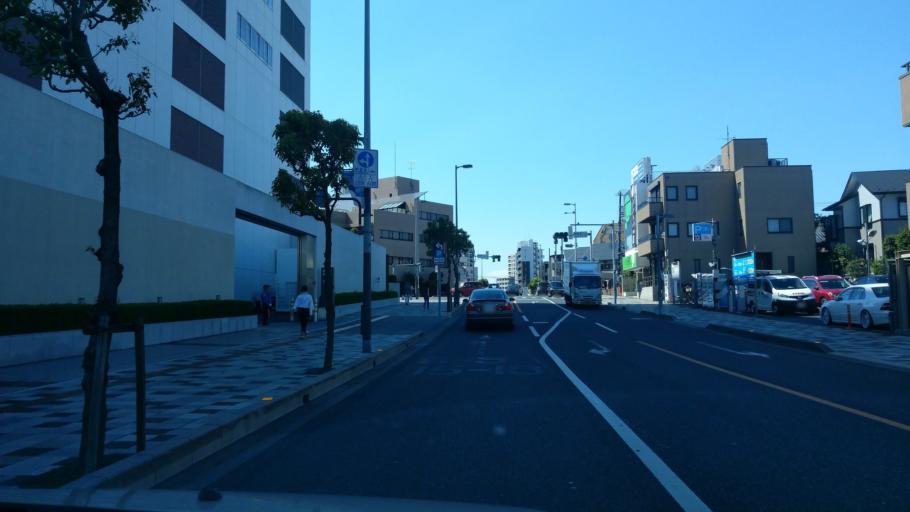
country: JP
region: Saitama
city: Yono
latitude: 35.8588
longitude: 139.6598
